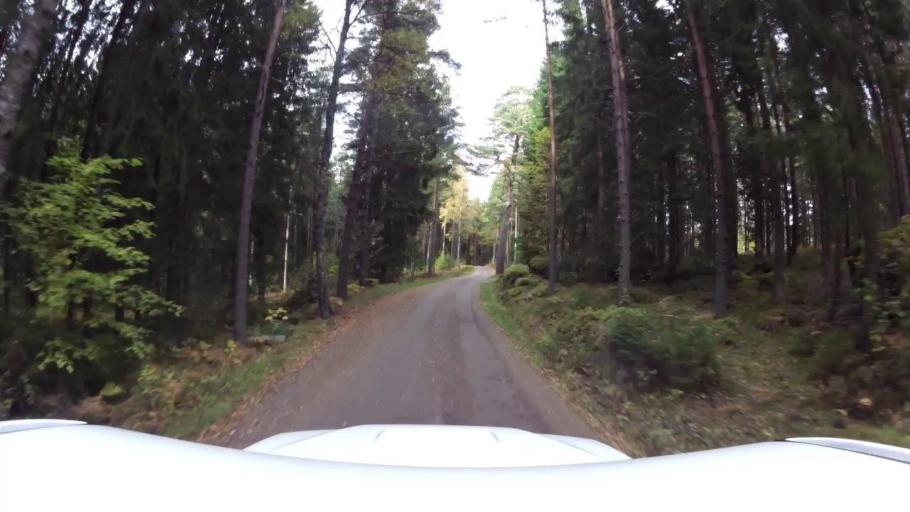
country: SE
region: OEstergoetland
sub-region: Linkopings Kommun
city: Ekangen
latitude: 58.5534
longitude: 15.6734
